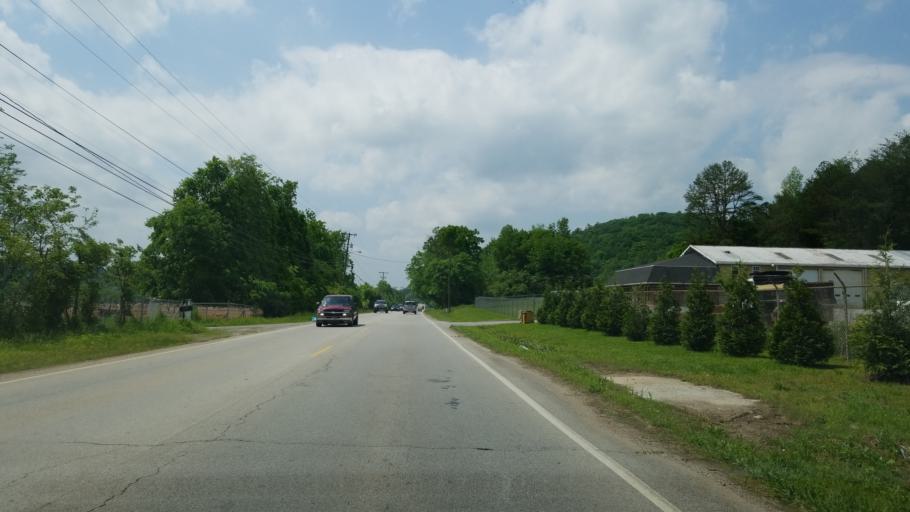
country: US
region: Tennessee
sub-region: Hamilton County
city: Falling Water
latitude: 35.2089
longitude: -85.2326
